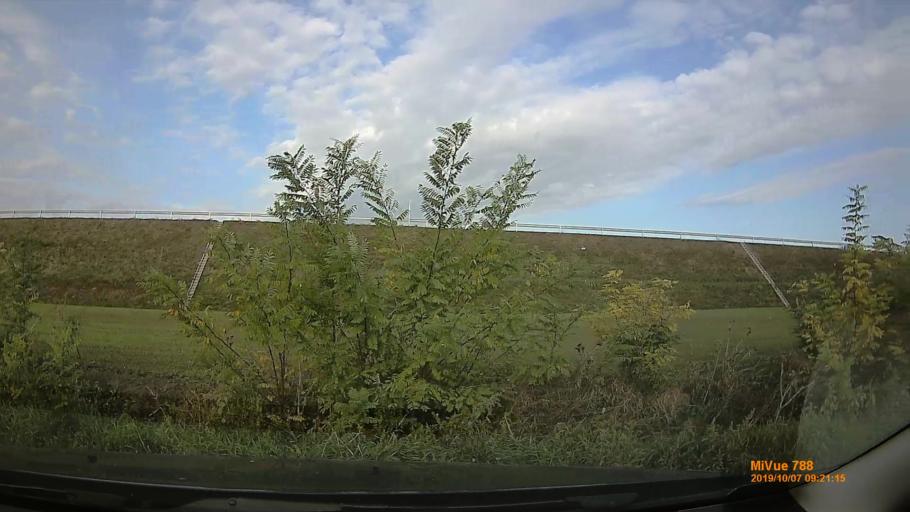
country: HU
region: Bekes
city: Szarvas
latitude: 46.8144
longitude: 20.6507
